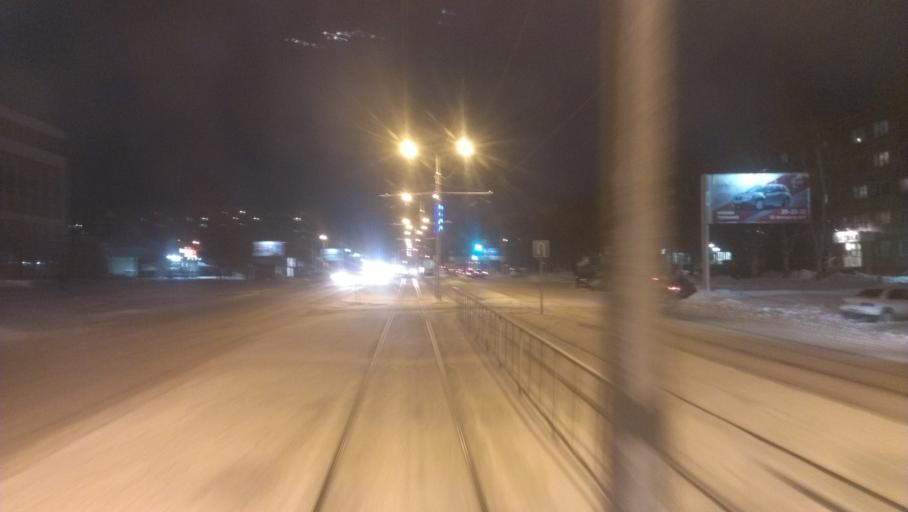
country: RU
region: Altai Krai
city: Novosilikatnyy
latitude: 53.3695
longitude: 83.6770
